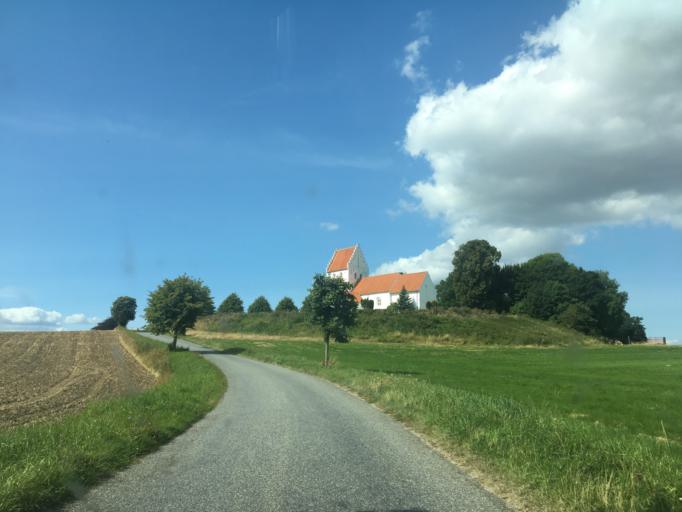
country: DK
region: South Denmark
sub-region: Middelfart Kommune
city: Ejby
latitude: 55.4043
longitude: 9.9153
